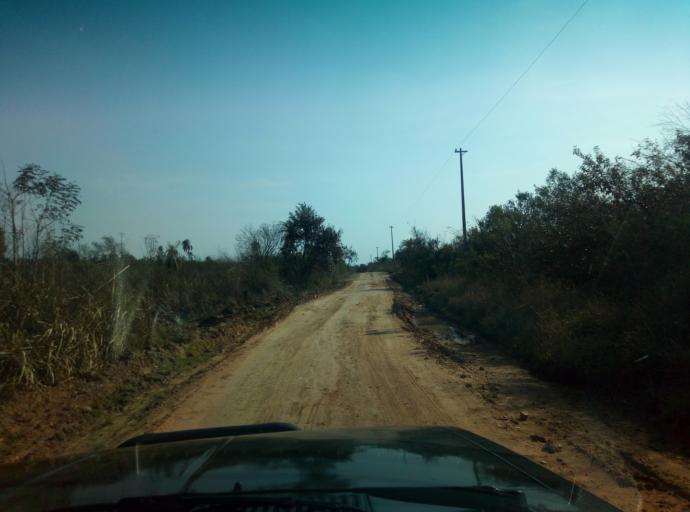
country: PY
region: Caaguazu
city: Doctor Cecilio Baez
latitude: -25.1865
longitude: -56.1918
